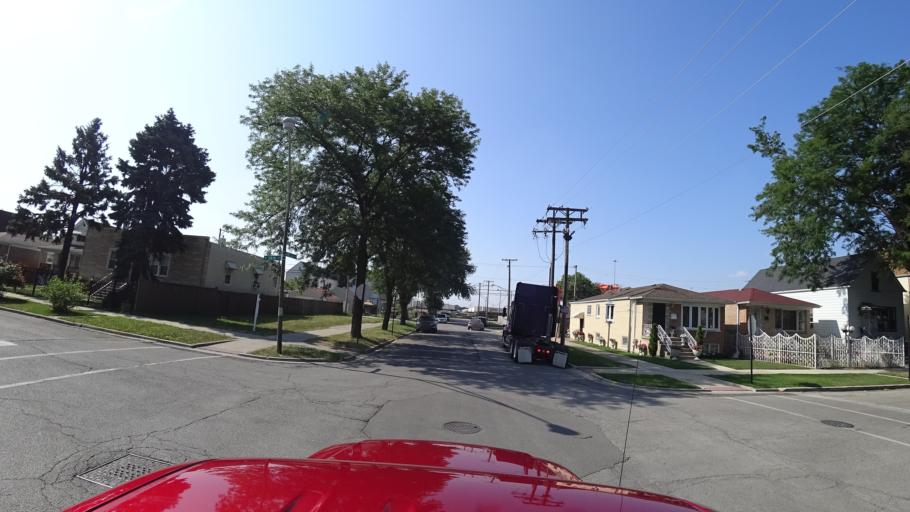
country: US
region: Illinois
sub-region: Cook County
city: Cicero
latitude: 41.8235
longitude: -87.7118
